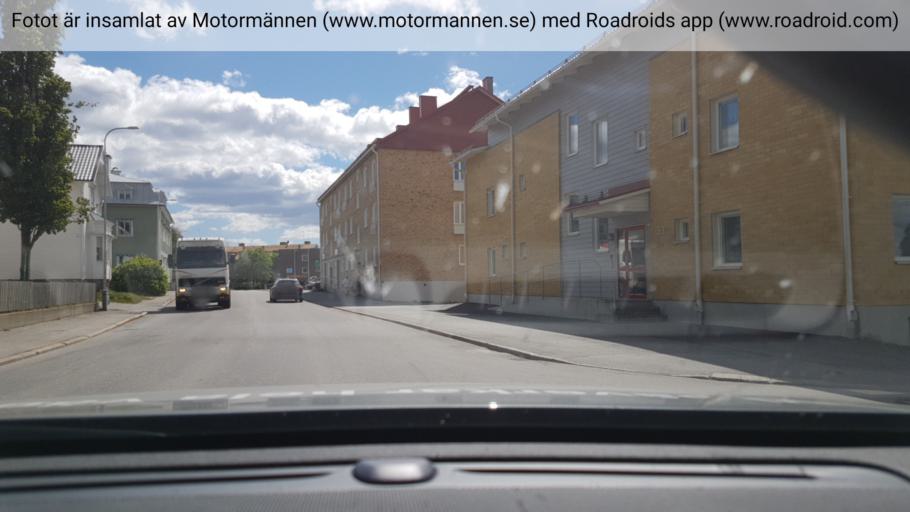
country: SE
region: Vaesterbotten
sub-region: Nordmalings Kommun
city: Nordmaling
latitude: 63.5714
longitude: 19.4962
